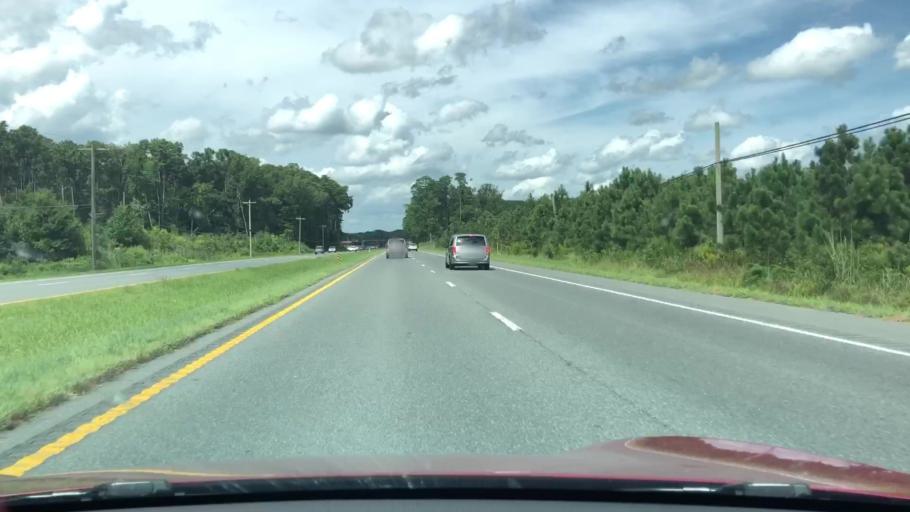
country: US
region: Virginia
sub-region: Accomack County
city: Wattsville
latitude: 37.9161
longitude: -75.5491
